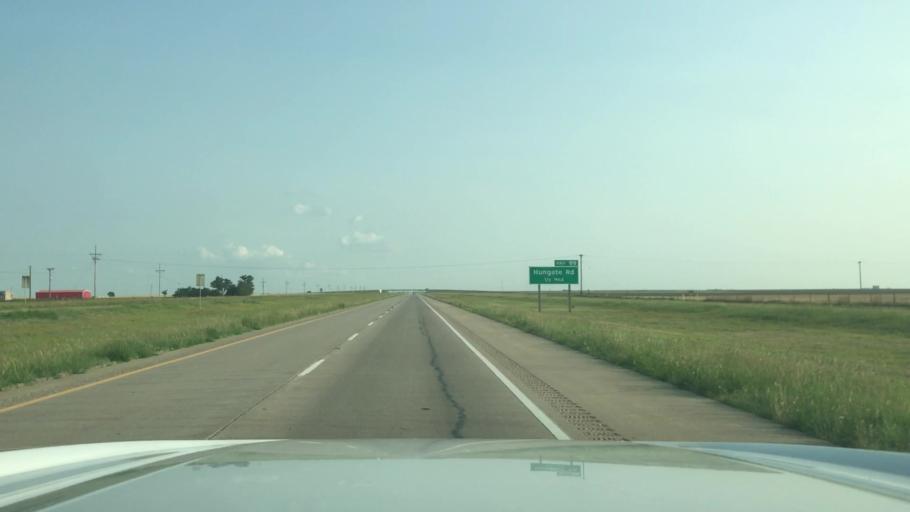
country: US
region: Texas
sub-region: Randall County
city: Canyon
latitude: 34.8993
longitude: -101.8487
